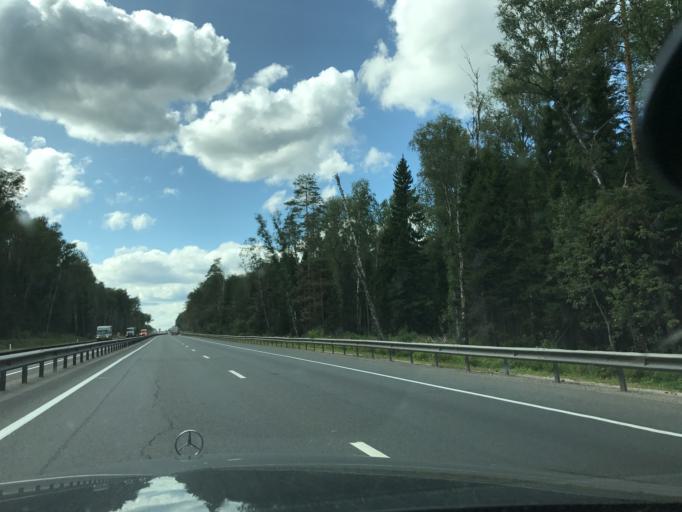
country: RU
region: Vladimir
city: Melekhovo
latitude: 56.2091
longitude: 41.2602
